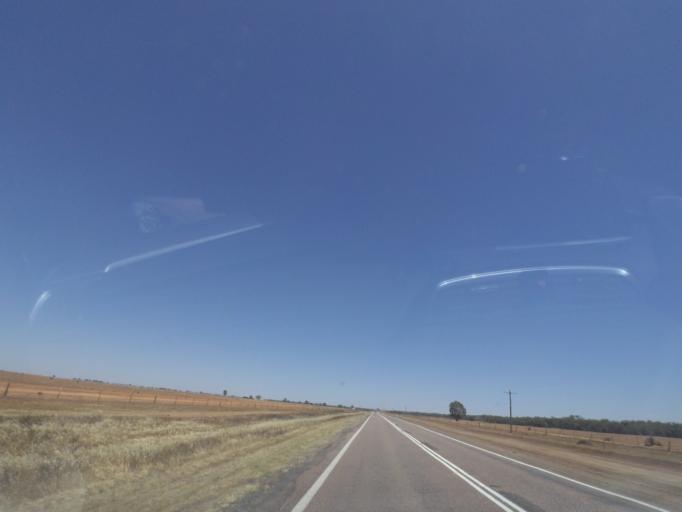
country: AU
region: New South Wales
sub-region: Berrigan
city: Berrigan
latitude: -35.1495
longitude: 145.9982
